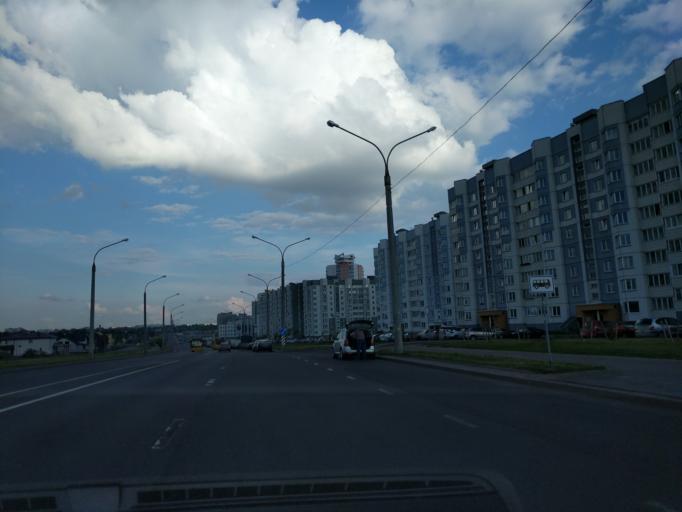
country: BY
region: Minsk
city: Zhdanovichy
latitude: 53.9345
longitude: 27.4346
